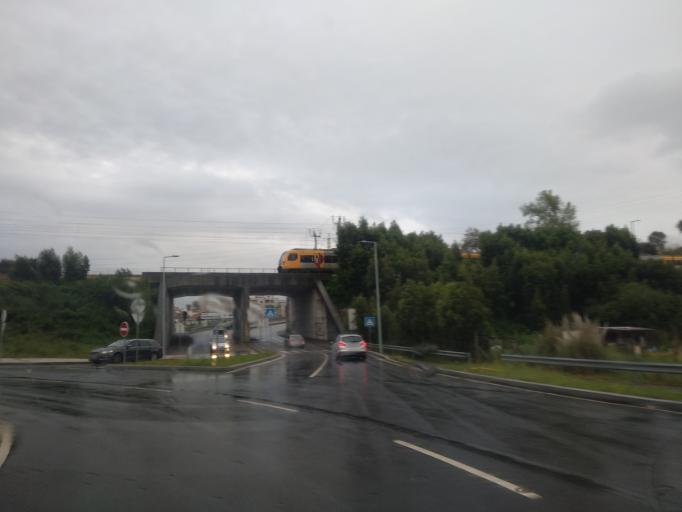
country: PT
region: Porto
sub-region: Gondomar
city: Rio Tinto
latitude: 41.1783
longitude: -8.5646
